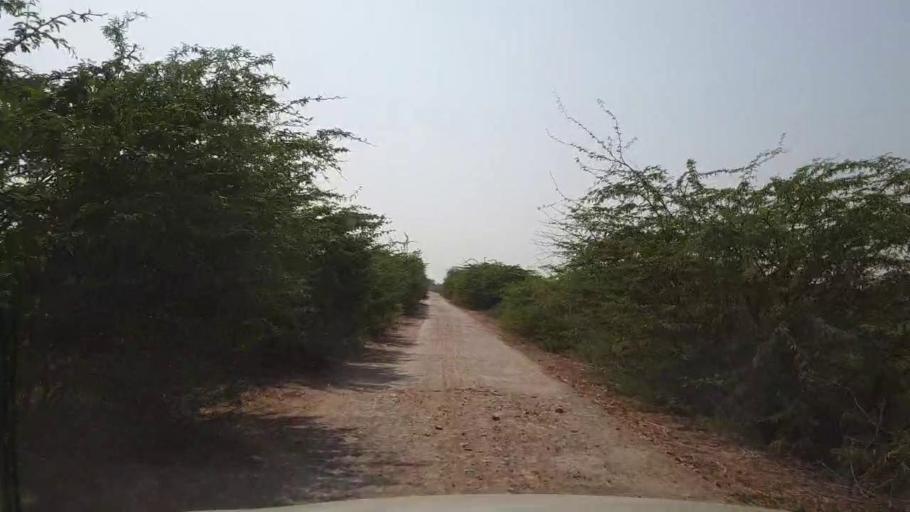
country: PK
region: Sindh
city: Dhoro Naro
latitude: 25.4563
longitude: 69.6246
